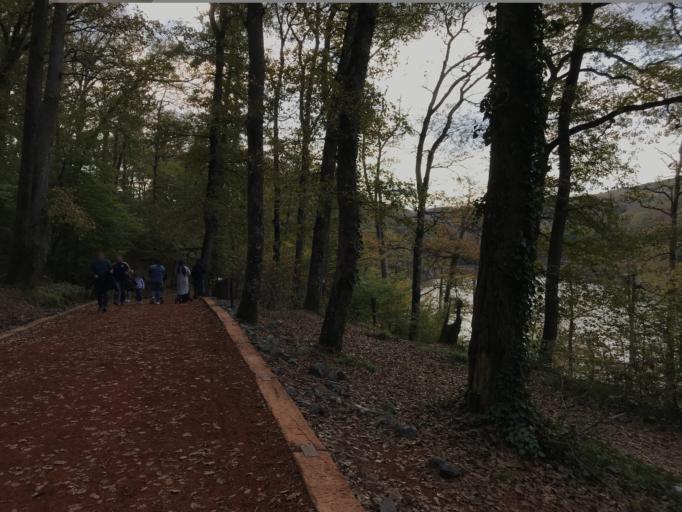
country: TR
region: Istanbul
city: Kemerburgaz
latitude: 41.1756
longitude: 28.9591
